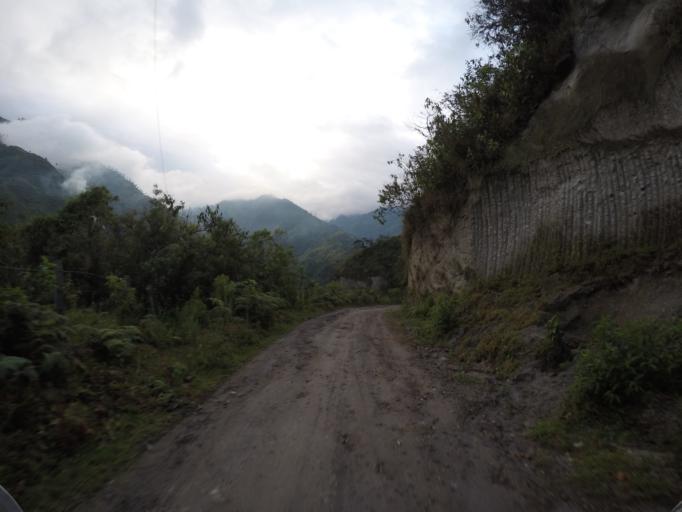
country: CO
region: Tolima
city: Cajamarca
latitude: 4.5188
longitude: -75.4073
